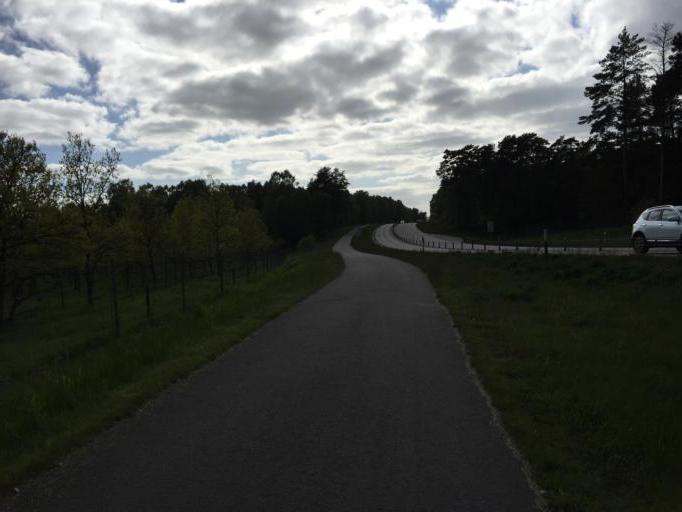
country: SE
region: Skane
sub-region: Sjobo Kommun
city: Blentarp
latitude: 55.6386
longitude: 13.5862
